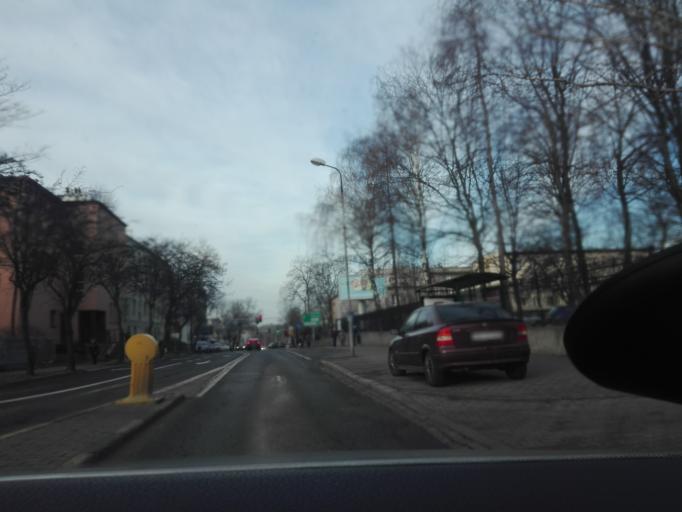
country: PL
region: Silesian Voivodeship
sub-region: Katowice
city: Katowice
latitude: 50.2712
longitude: 19.0209
